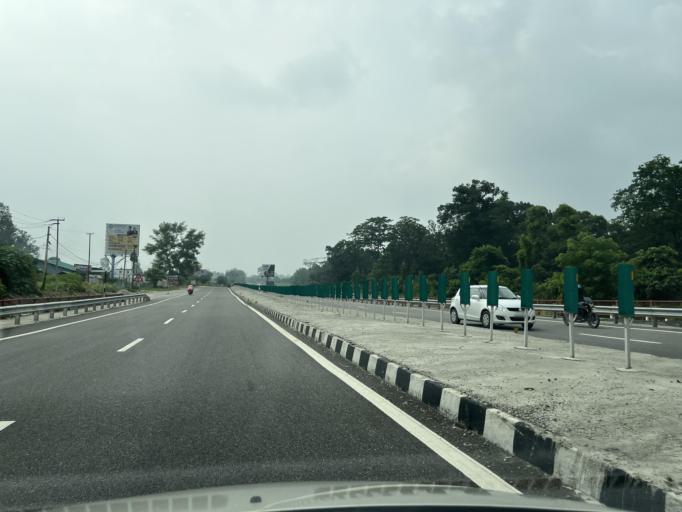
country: IN
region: Uttarakhand
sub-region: Dehradun
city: Raiwala
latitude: 30.0635
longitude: 78.2106
